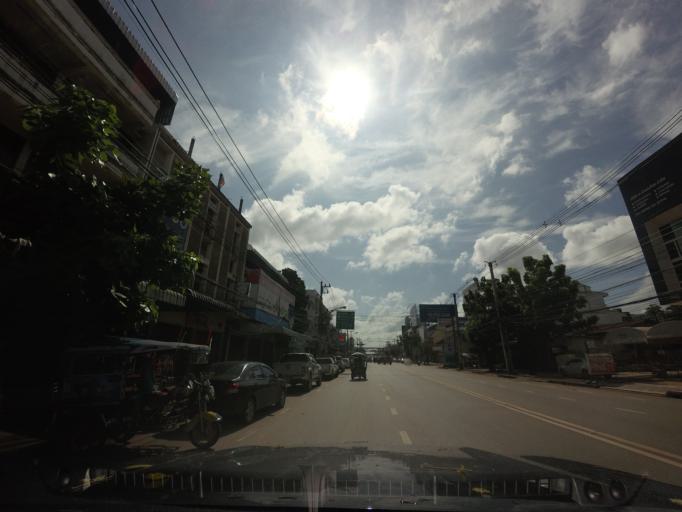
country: TH
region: Changwat Udon Thani
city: Udon Thani
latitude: 17.3993
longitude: 102.8029
